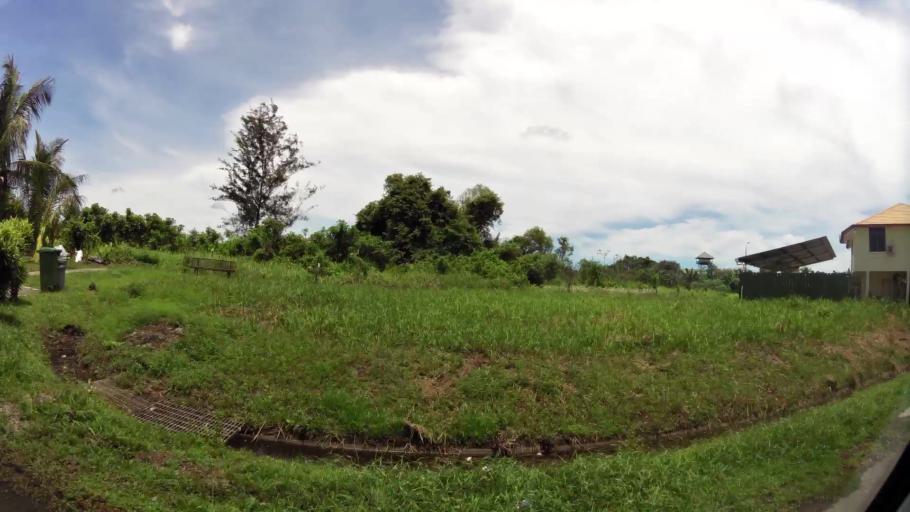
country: BN
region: Belait
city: Kuala Belait
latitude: 4.5883
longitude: 114.2450
